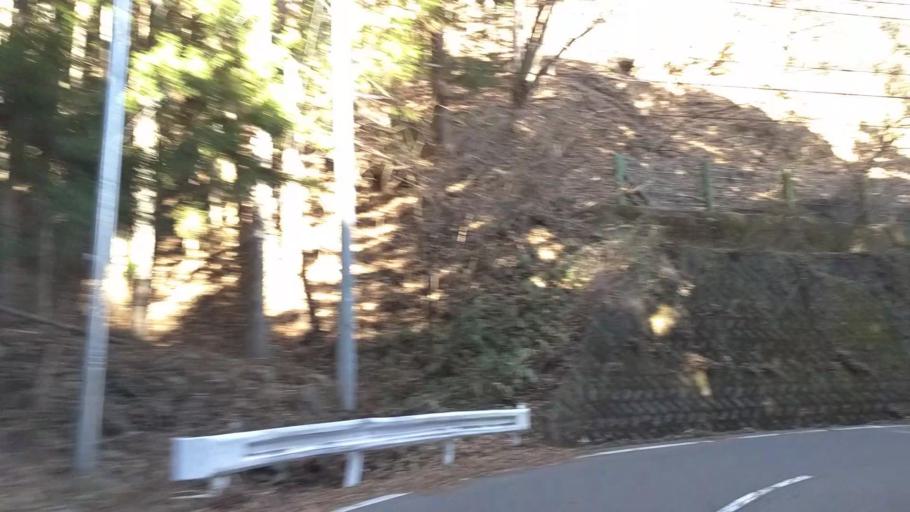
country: JP
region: Yamanashi
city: Otsuki
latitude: 35.5134
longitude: 138.9812
